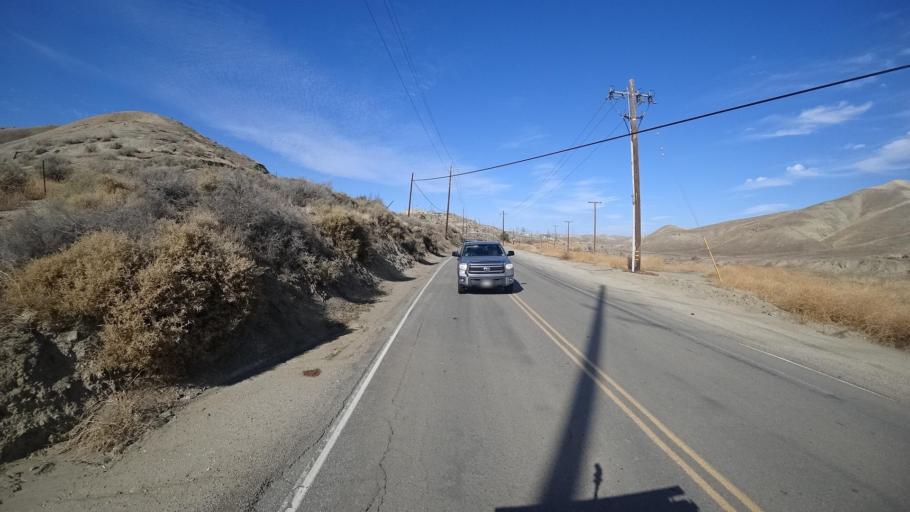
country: US
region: California
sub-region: Kern County
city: Oildale
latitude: 35.5535
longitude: -118.9586
